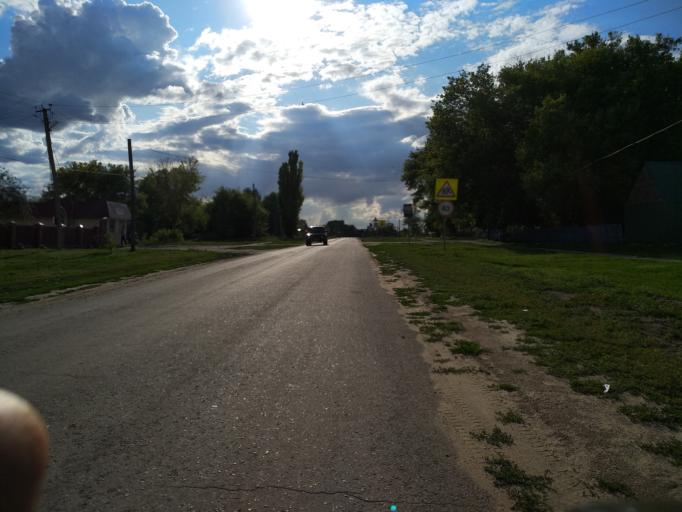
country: RU
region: Lipetsk
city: Dobrinka
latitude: 52.0379
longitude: 40.5468
